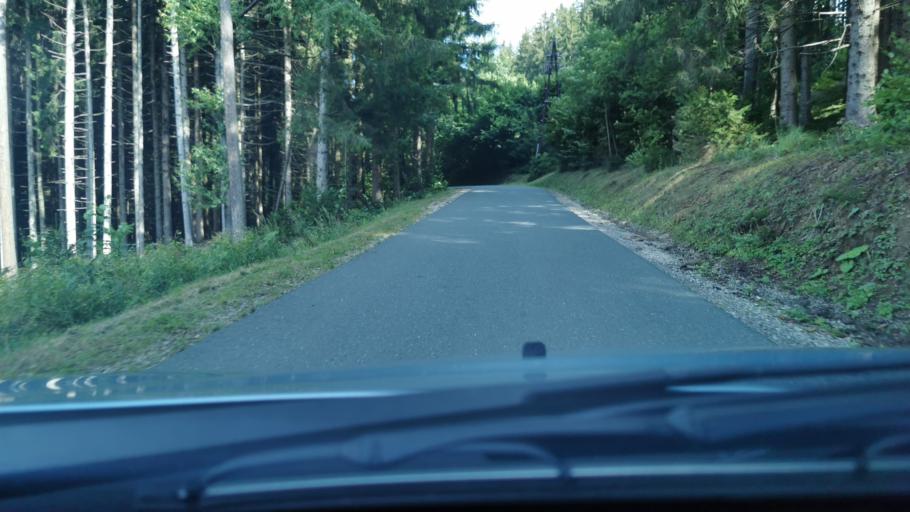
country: AT
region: Styria
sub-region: Politischer Bezirk Weiz
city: Baierdorf-Umgebung
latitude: 47.3073
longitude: 15.7068
